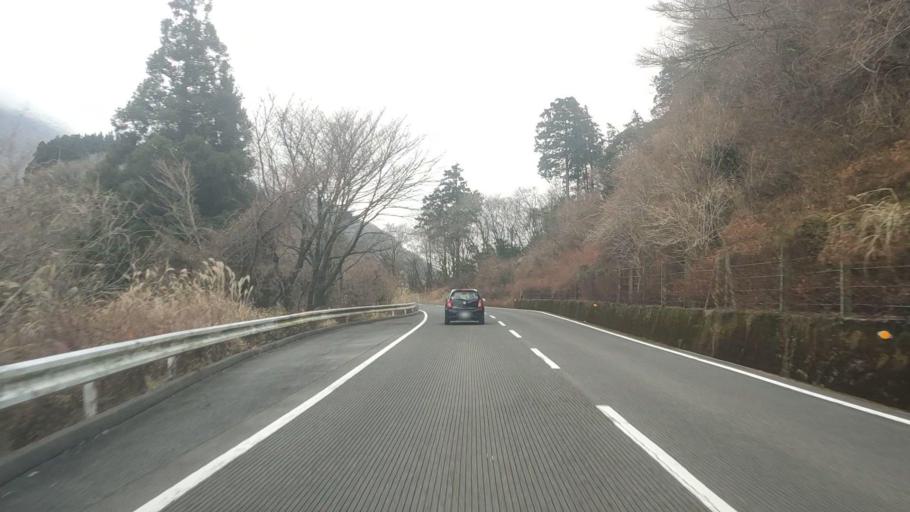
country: JP
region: Nagasaki
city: Shimabara
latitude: 32.7656
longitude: 130.2721
